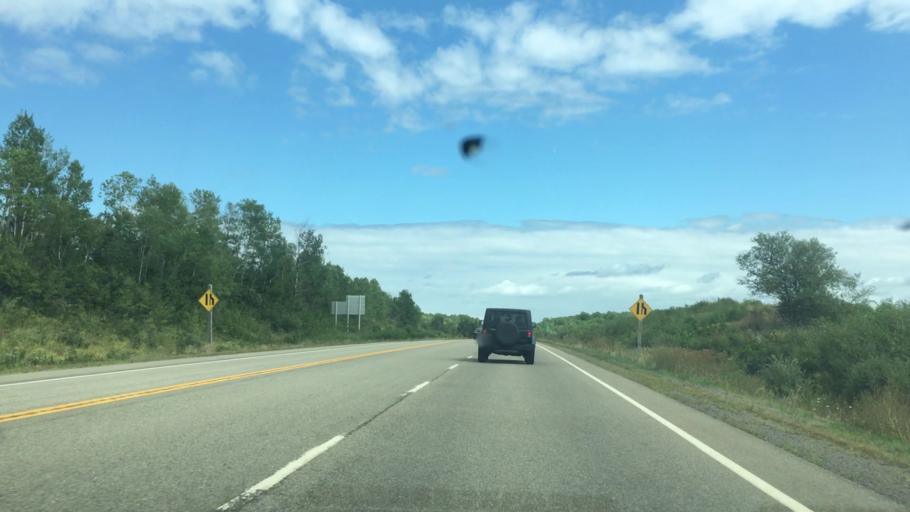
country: CA
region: Nova Scotia
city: Port Hawkesbury
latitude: 45.6246
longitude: -61.6028
